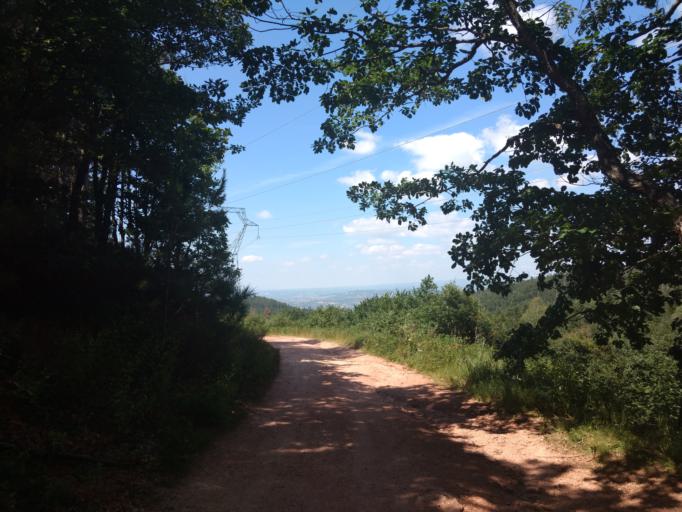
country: FR
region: Midi-Pyrenees
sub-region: Departement de l'Aveyron
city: Laissac
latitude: 44.3646
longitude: 2.7575
